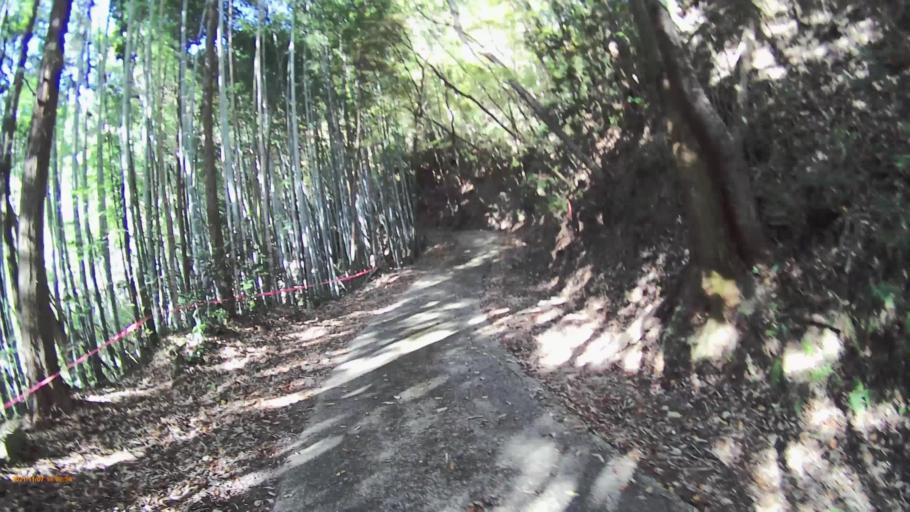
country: JP
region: Gifu
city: Mitake
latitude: 35.4251
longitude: 137.1871
